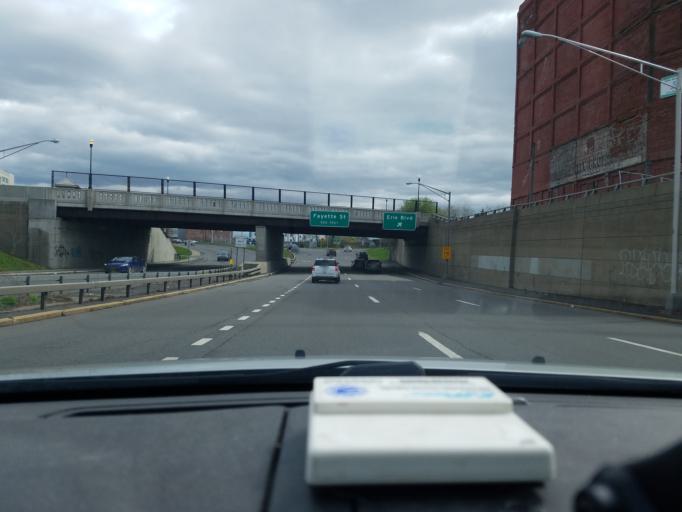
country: US
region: New York
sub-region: Onondaga County
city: Syracuse
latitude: 43.0512
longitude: -76.1590
